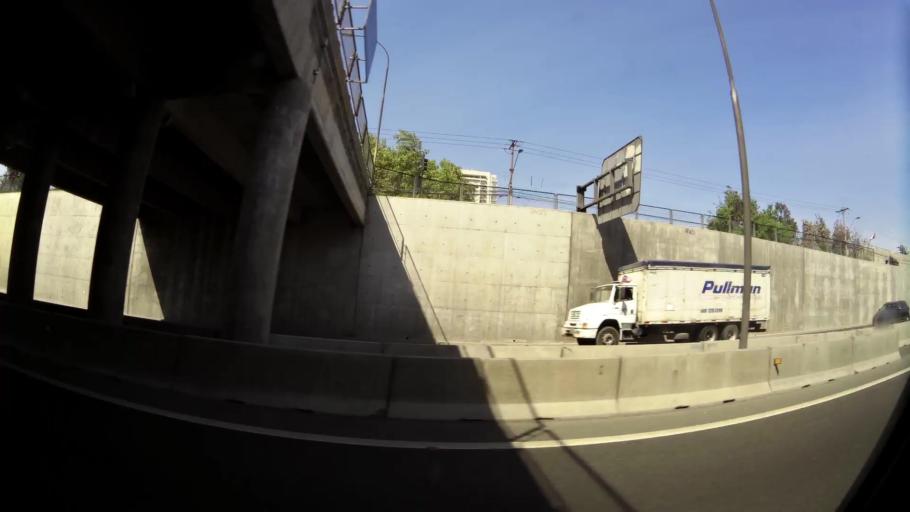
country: CL
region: Santiago Metropolitan
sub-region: Provincia de Santiago
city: Santiago
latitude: -33.4964
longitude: -70.6643
